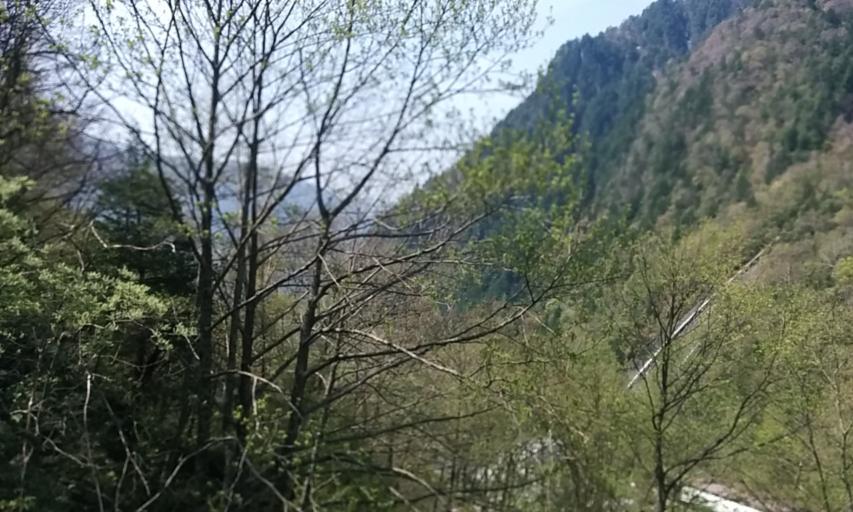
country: JP
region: Nagano
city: Hotaka
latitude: 36.2854
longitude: 137.5763
